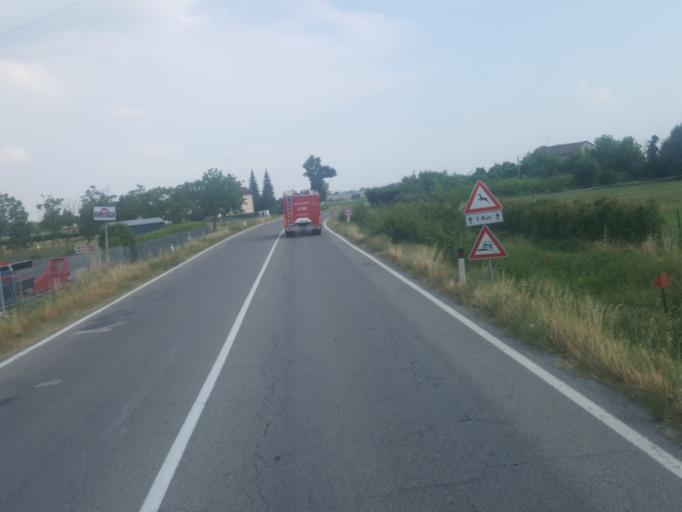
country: IT
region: Emilia-Romagna
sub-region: Provincia di Modena
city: Gaggio
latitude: 44.6159
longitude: 11.0141
